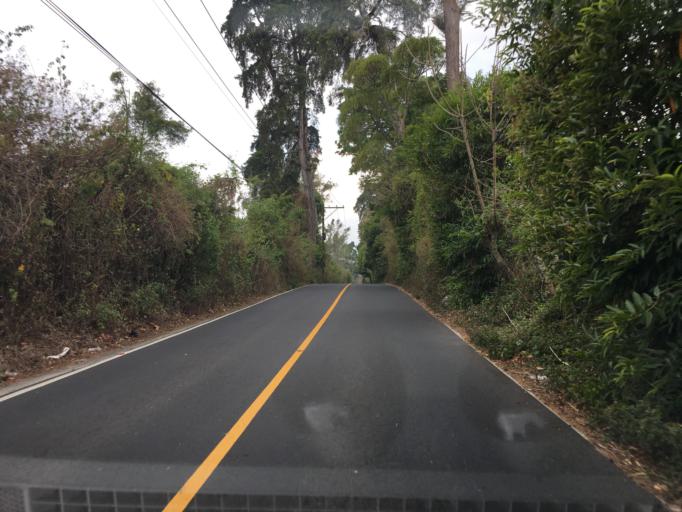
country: GT
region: Guatemala
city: Villa Canales
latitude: 14.4357
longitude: -90.5097
